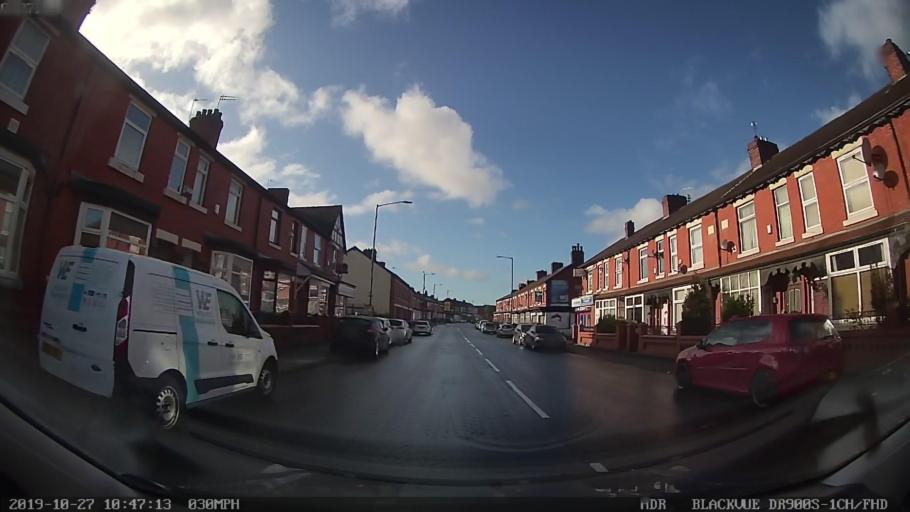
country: GB
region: England
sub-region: Manchester
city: Blackley
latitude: 53.5151
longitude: -2.1920
